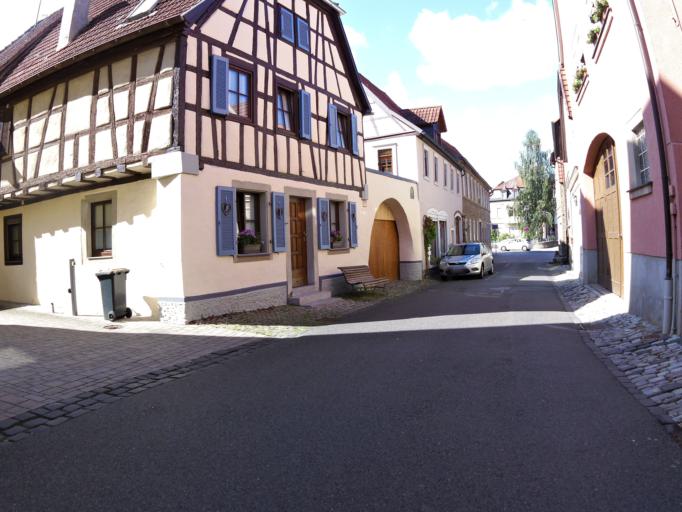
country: DE
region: Bavaria
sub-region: Regierungsbezirk Unterfranken
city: Dettelbach
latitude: 49.8014
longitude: 10.1615
